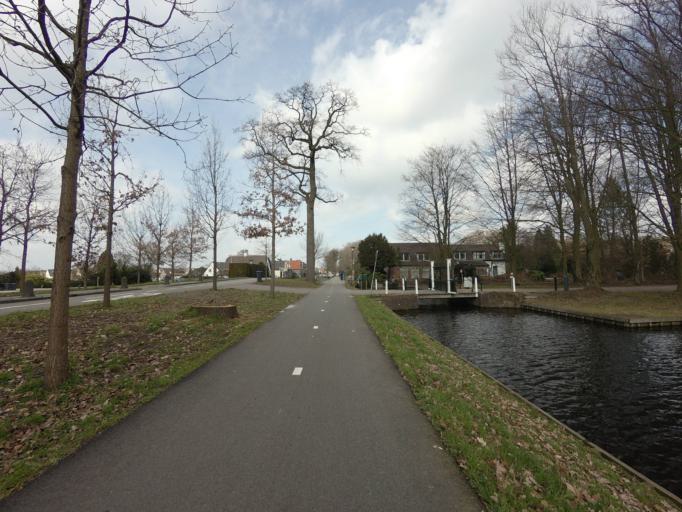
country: NL
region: North Holland
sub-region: Gemeente Wijdemeren
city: Kortenhoef
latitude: 52.2322
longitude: 5.1221
